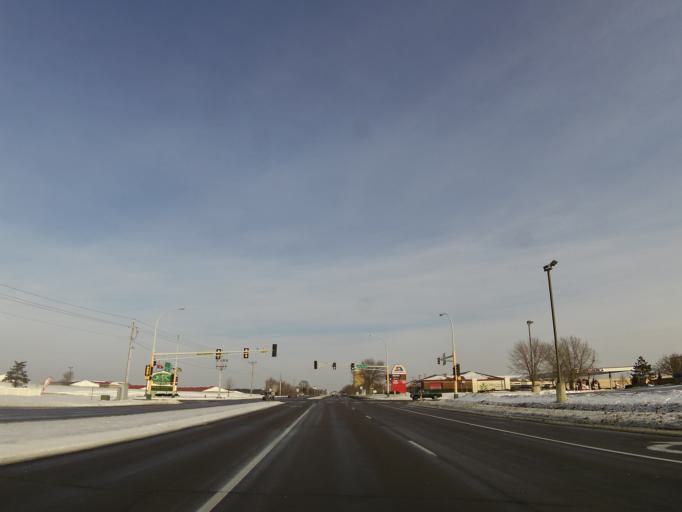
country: US
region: Minnesota
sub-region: Scott County
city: Shakopee
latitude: 44.7842
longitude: -93.4696
